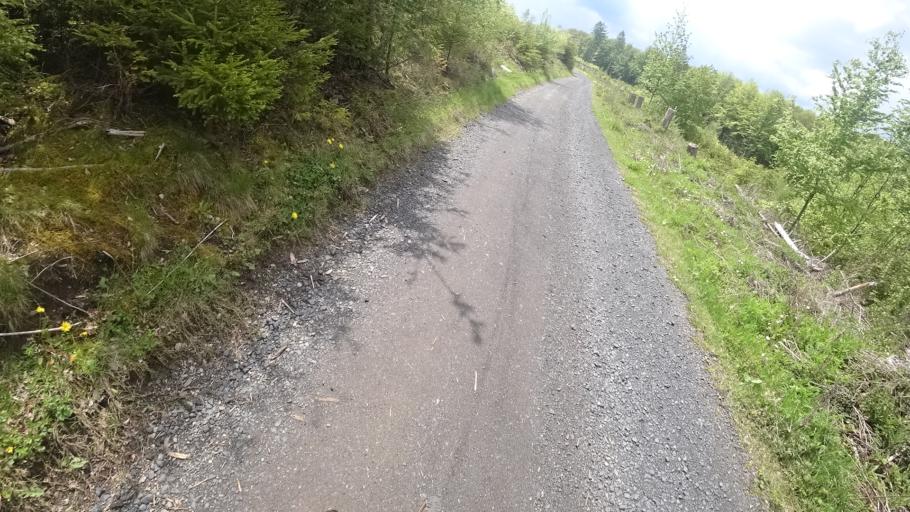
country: DE
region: Rheinland-Pfalz
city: Scheuerfeld
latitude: 50.7798
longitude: 7.8443
